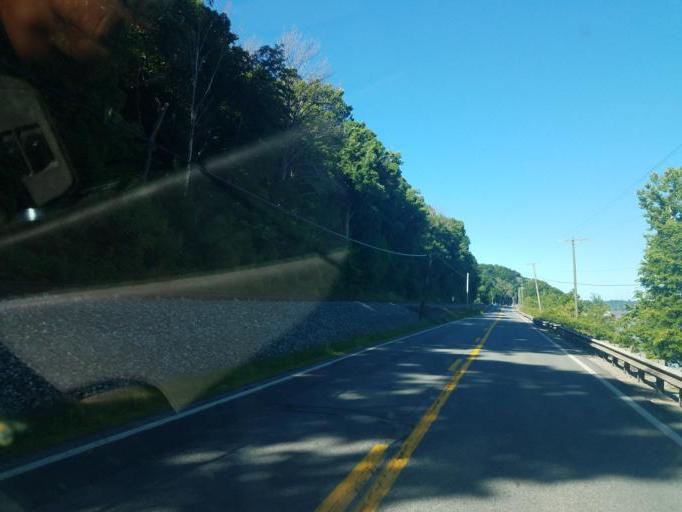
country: US
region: West Virginia
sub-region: Mason County
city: Point Pleasant
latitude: 38.8217
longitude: -82.1579
